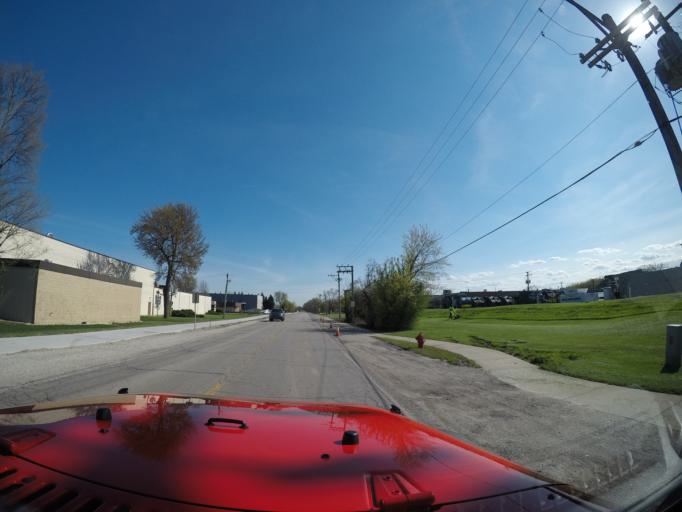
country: US
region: Illinois
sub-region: Cook County
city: Northbrook
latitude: 42.1020
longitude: -87.8294
